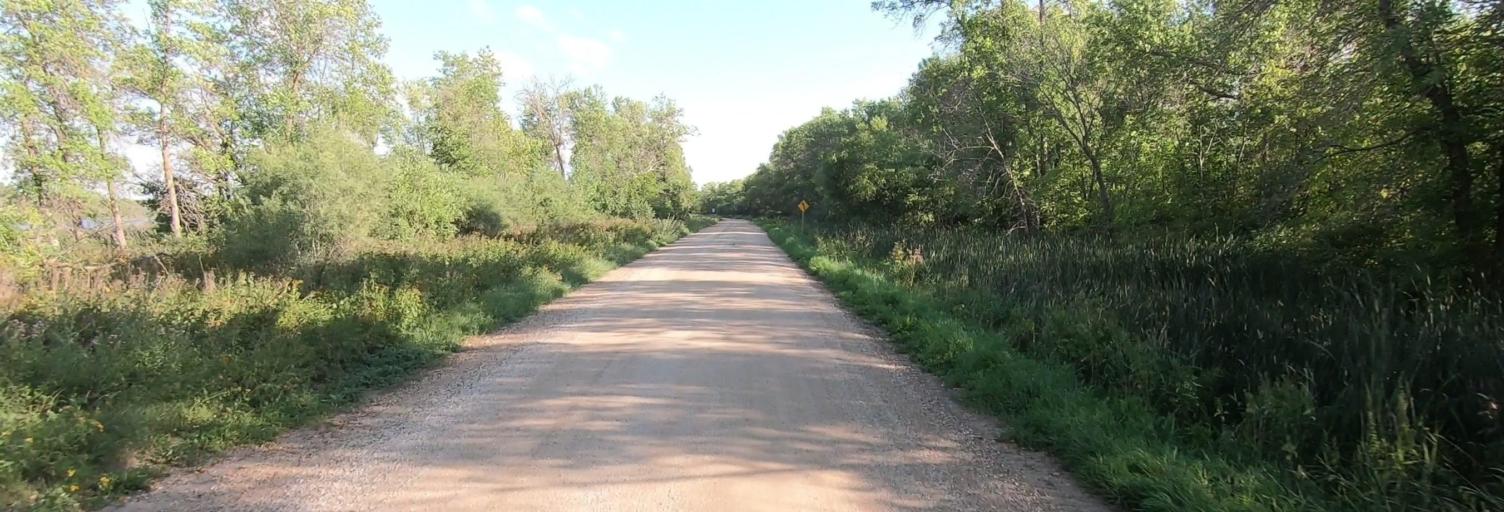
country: CA
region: Manitoba
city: Selkirk
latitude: 50.2902
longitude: -96.8662
